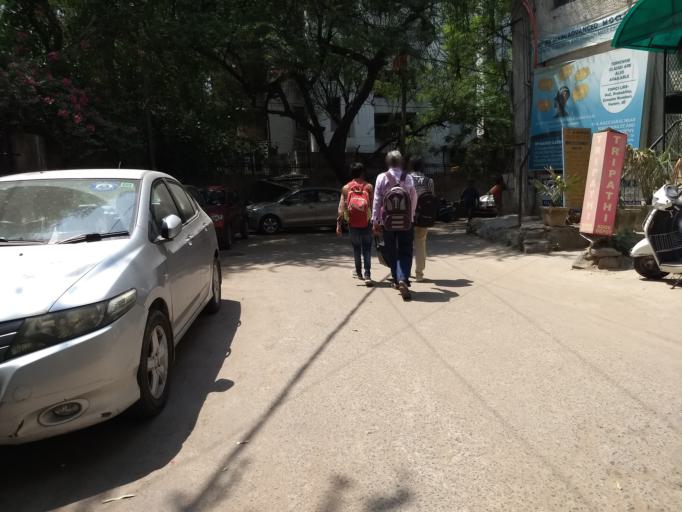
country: IN
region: NCT
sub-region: New Delhi
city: New Delhi
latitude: 28.5414
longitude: 77.2029
